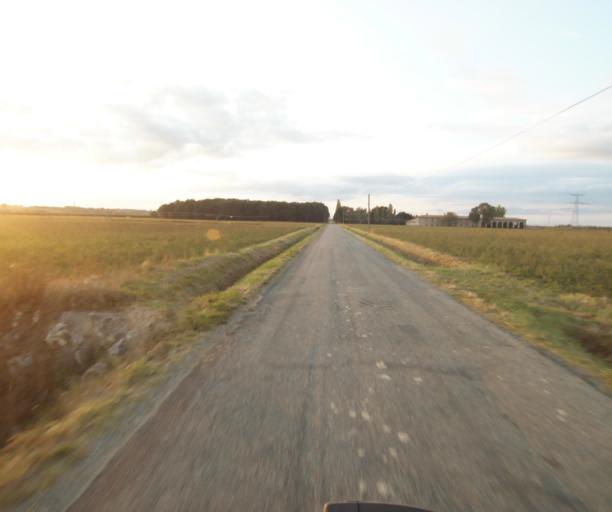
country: FR
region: Midi-Pyrenees
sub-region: Departement du Tarn-et-Garonne
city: Verdun-sur-Garonne
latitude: 43.8270
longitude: 1.2333
